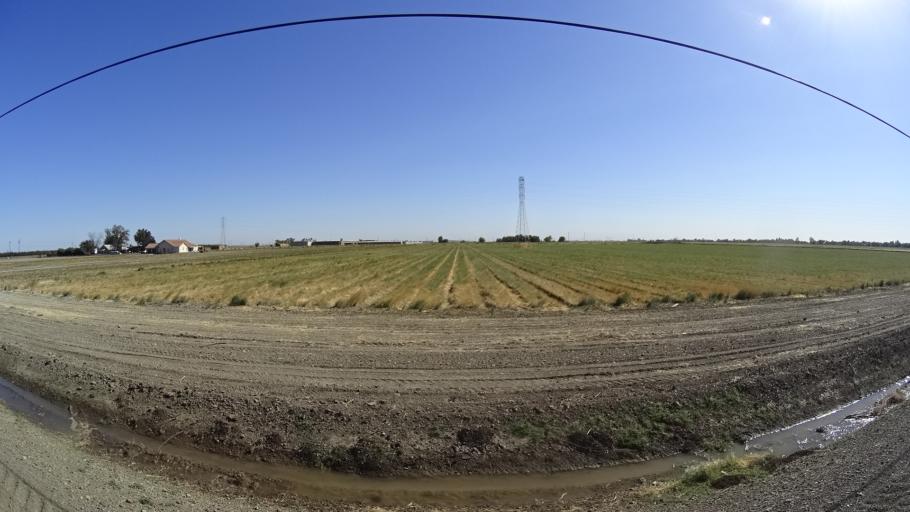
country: US
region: California
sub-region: Yolo County
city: Cottonwood
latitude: 38.6181
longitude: -121.9714
